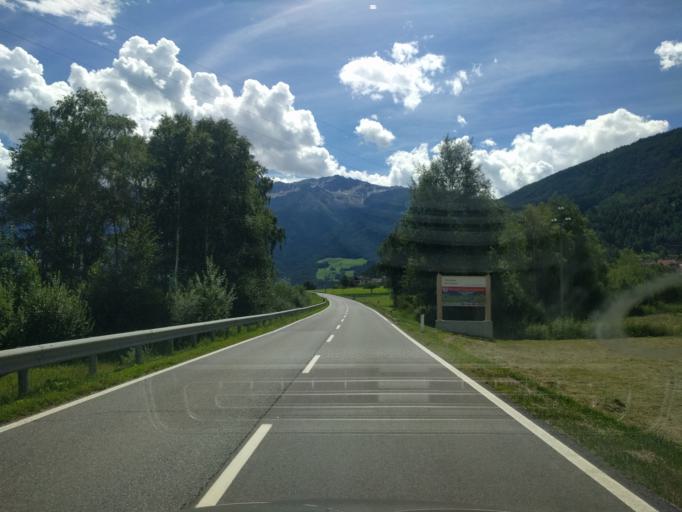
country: IT
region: Trentino-Alto Adige
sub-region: Bolzano
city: Sluderno
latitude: 46.6414
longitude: 10.5701
